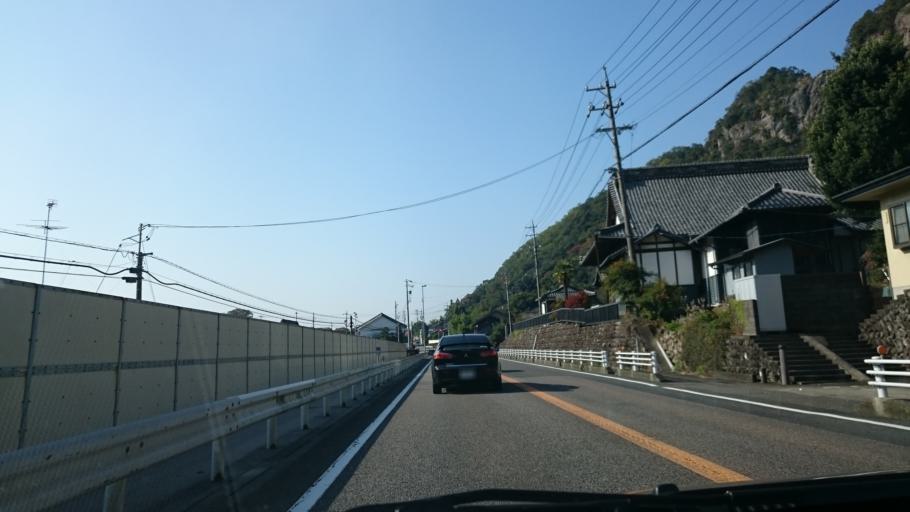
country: JP
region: Gifu
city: Minokamo
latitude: 35.5219
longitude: 137.0943
